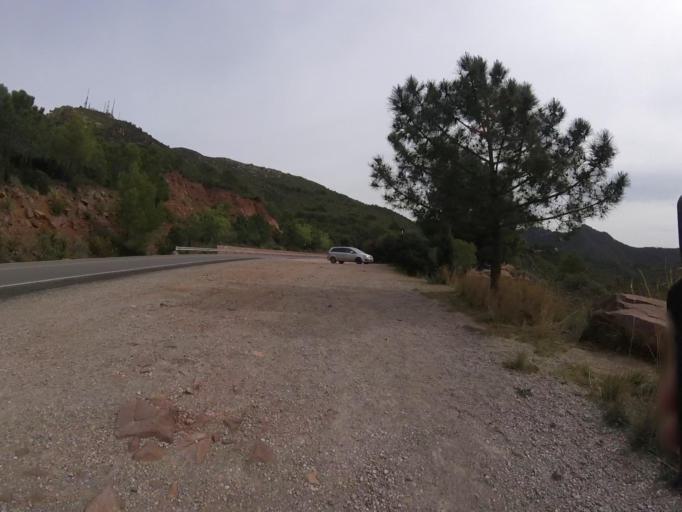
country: ES
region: Valencia
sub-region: Provincia de Castello
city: Benicassim
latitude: 40.0777
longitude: 0.0306
